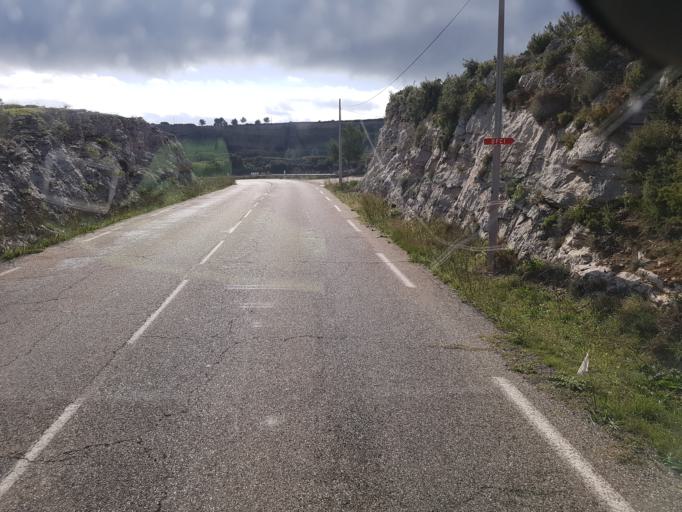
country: FR
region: Provence-Alpes-Cote d'Azur
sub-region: Departement des Bouches-du-Rhone
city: Le Rove
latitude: 43.3571
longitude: 5.2304
